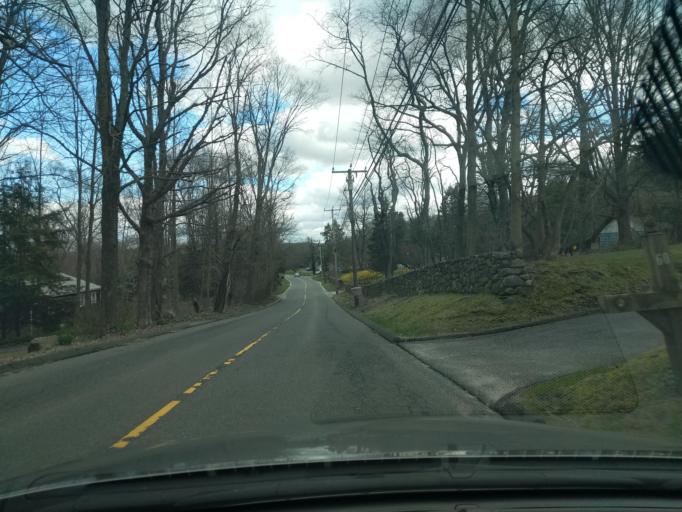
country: US
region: Connecticut
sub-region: Fairfield County
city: Bethel
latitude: 41.3920
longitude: -73.3732
